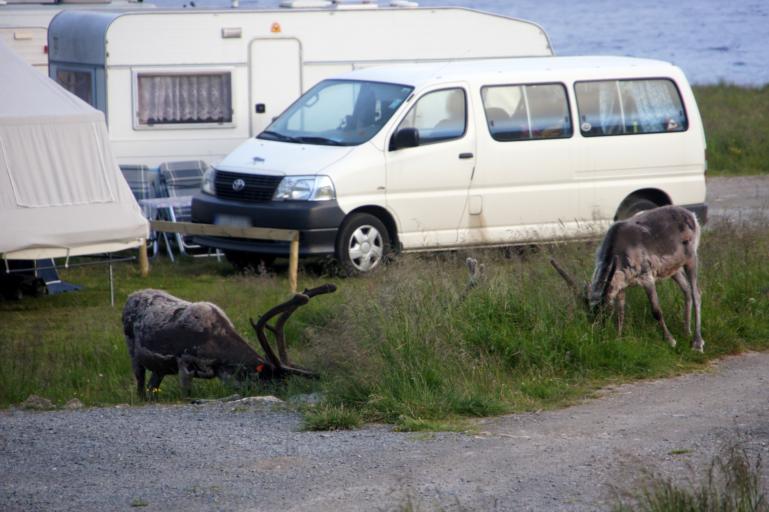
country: NO
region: Finnmark Fylke
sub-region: Nordkapp
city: Honningsvag
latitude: 71.1079
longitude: 25.8115
